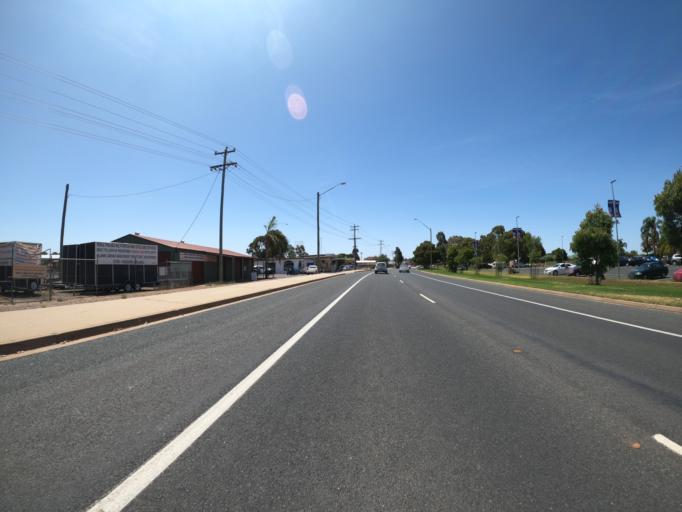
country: AU
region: New South Wales
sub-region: Corowa Shire
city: Mulwala
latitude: -35.9945
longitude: 146.0013
